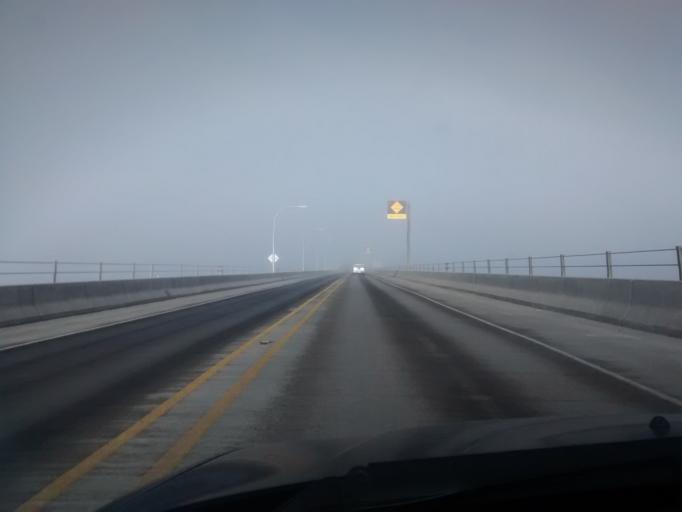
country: US
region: Washington
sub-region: Kitsap County
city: Lofall
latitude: 47.8550
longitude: -122.6158
